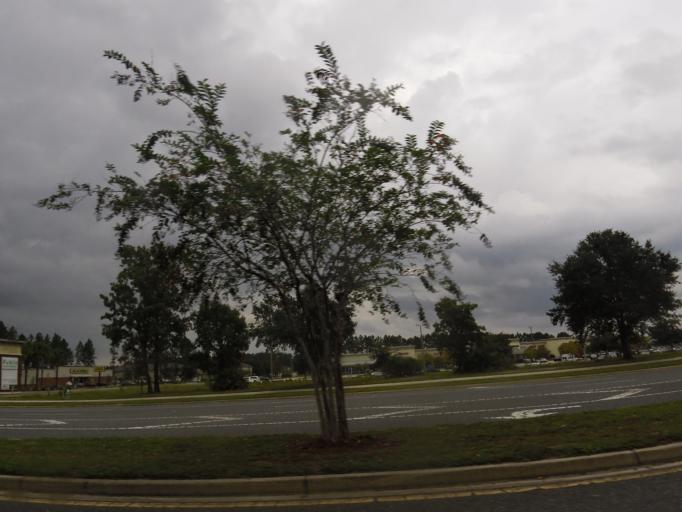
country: US
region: Florida
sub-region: Clay County
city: Lakeside
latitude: 30.1604
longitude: -81.8381
